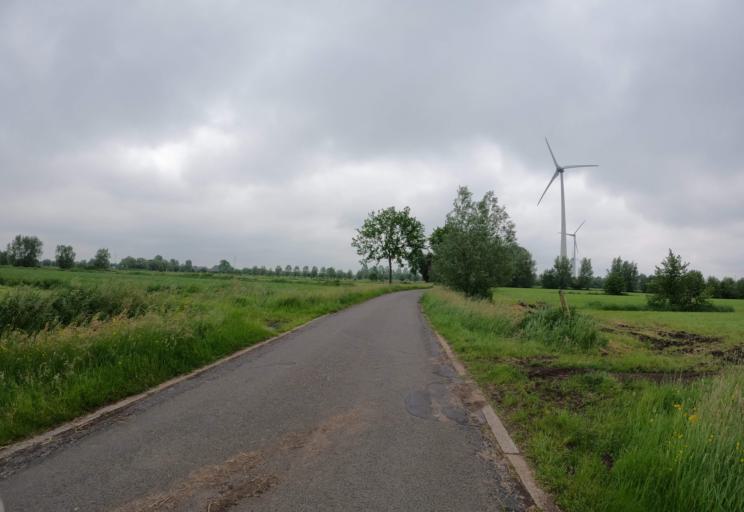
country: BE
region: Flanders
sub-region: Provincie Oost-Vlaanderen
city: Zele
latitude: 51.0579
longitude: 4.0629
